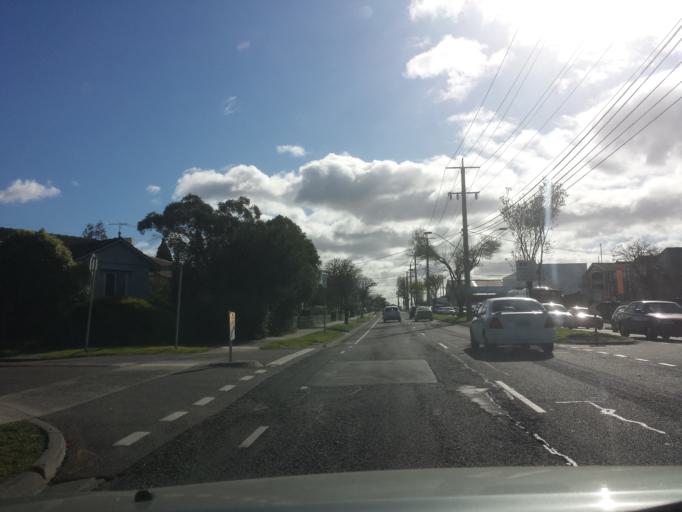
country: AU
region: Victoria
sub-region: Darebin
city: Preston
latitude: -37.7455
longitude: 145.0220
